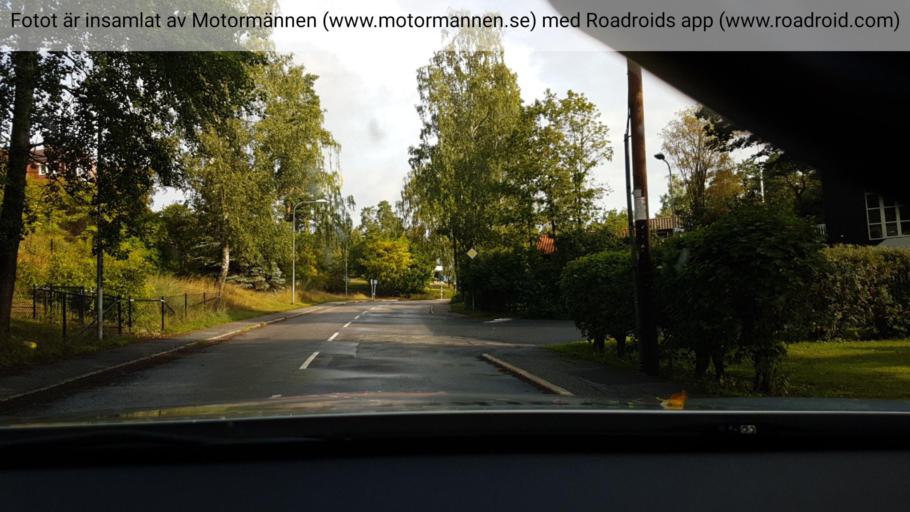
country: SE
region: Stockholm
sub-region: Lidingo
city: Brevik
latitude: 59.3528
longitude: 18.2291
